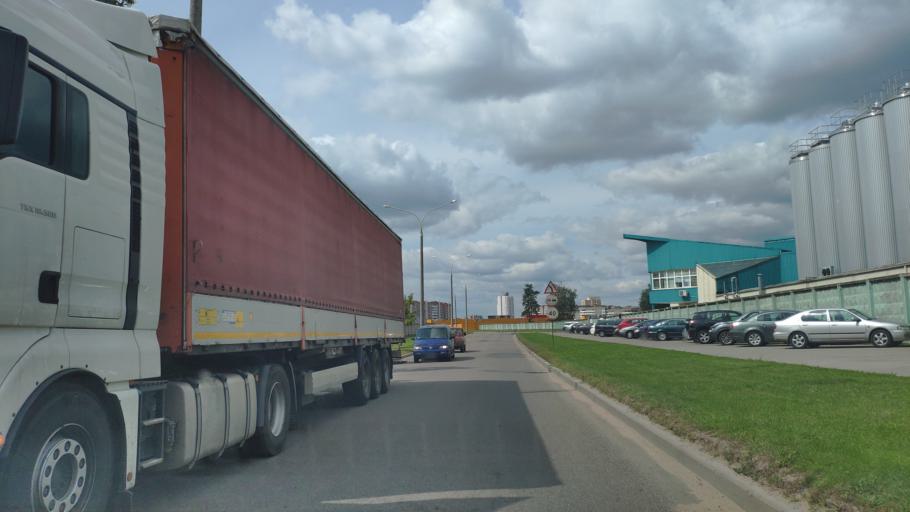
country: BY
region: Minsk
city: Vyaliki Trastsyanets
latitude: 53.8652
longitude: 27.6974
